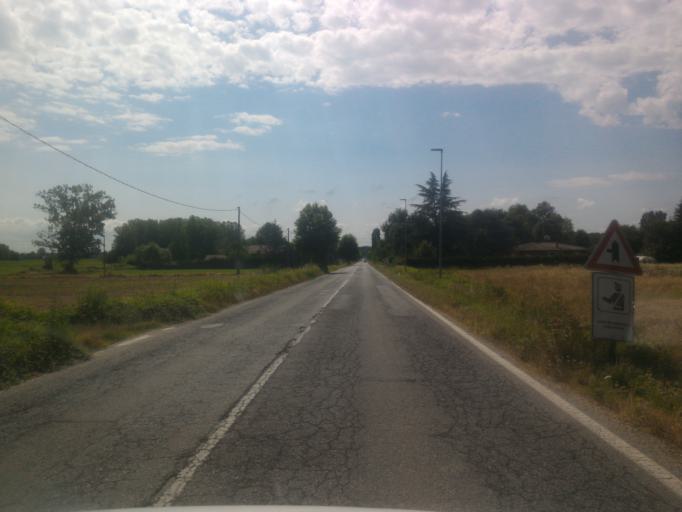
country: IT
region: Piedmont
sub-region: Provincia di Torino
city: Cumiana
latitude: 44.9649
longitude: 7.3969
